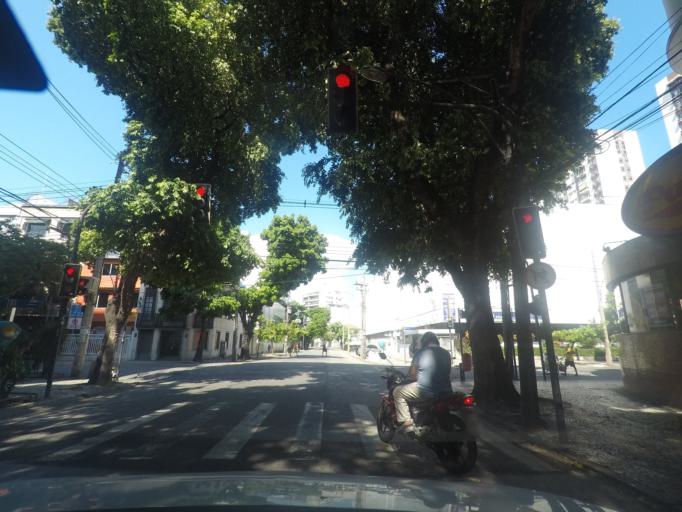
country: BR
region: Rio de Janeiro
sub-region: Rio De Janeiro
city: Rio de Janeiro
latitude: -22.9163
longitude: -43.2186
